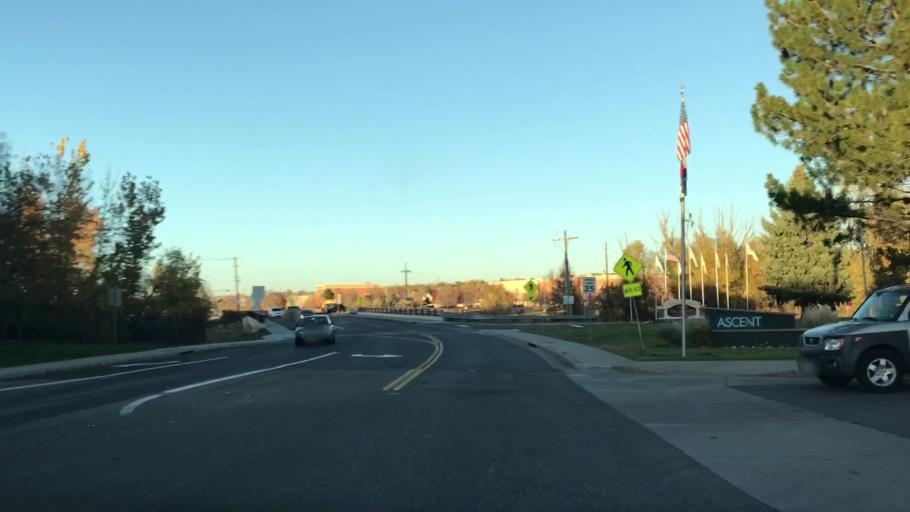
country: US
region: Colorado
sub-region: Arapahoe County
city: Glendale
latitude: 39.6697
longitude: -104.8906
